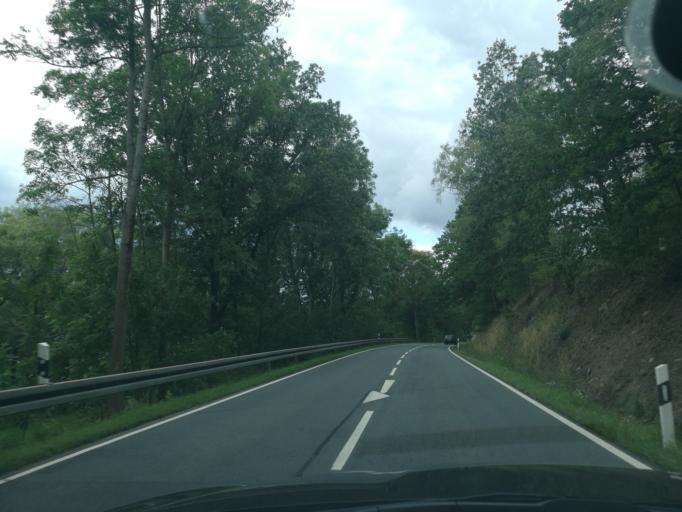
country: DE
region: Saxony
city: Eichigt
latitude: 50.3693
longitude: 12.2127
